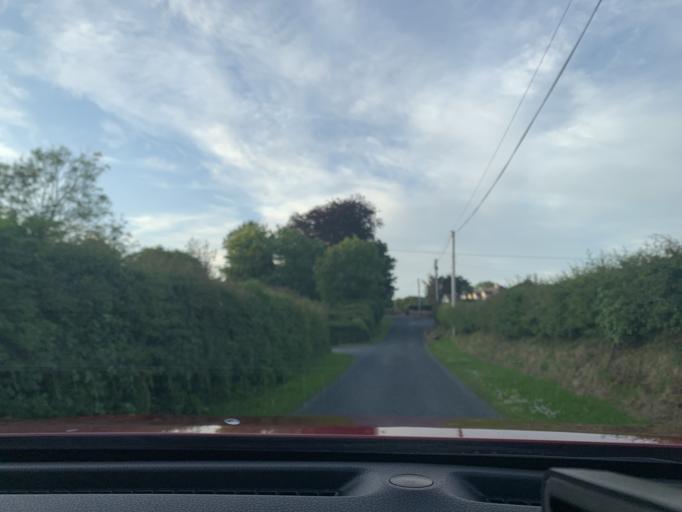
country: IE
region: Connaught
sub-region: Sligo
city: Sligo
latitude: 54.2856
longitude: -8.4318
